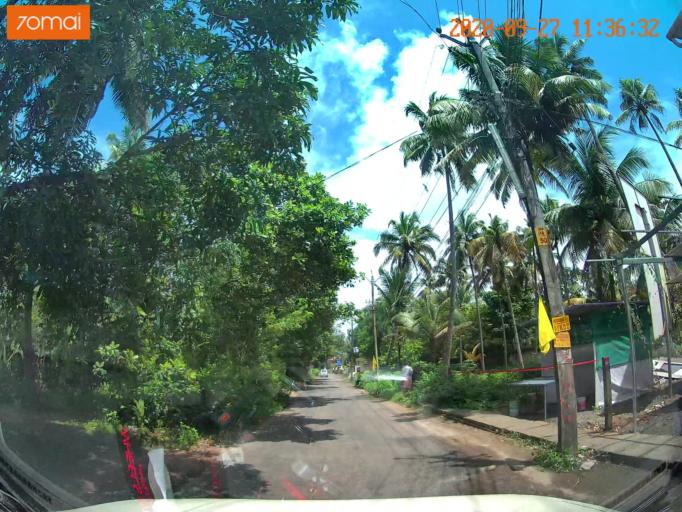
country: IN
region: Kerala
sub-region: Thrissur District
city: Thanniyam
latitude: 10.4501
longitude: 76.1246
